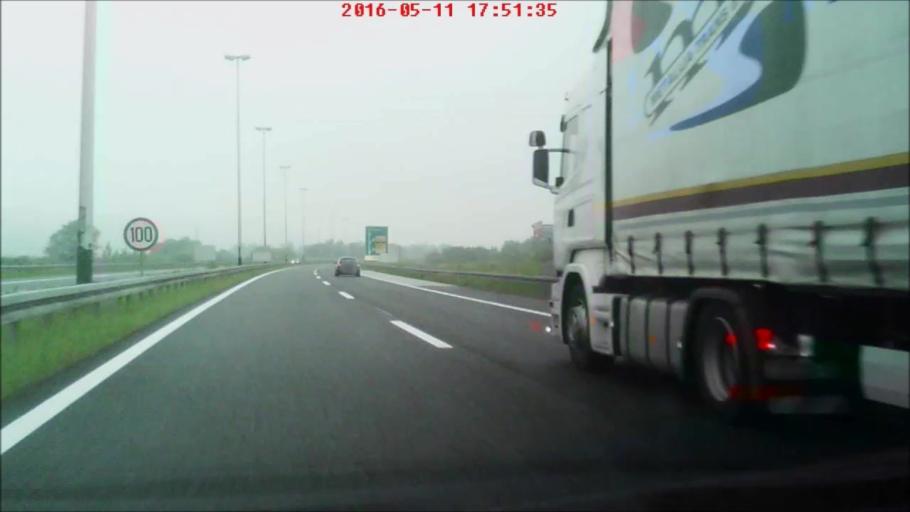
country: HR
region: Zagrebacka
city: Zapresic
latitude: 45.8638
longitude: 15.8316
